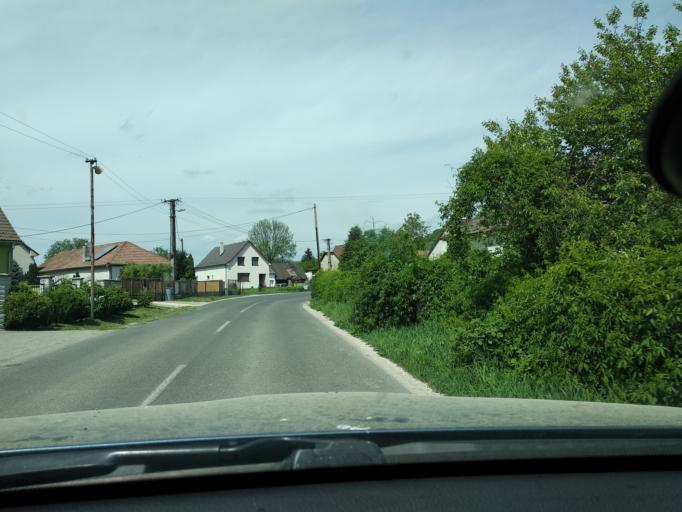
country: SK
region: Trenciansky
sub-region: Okres Nove Mesto nad Vahom
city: Nove Mesto nad Vahom
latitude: 48.8030
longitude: 17.8581
